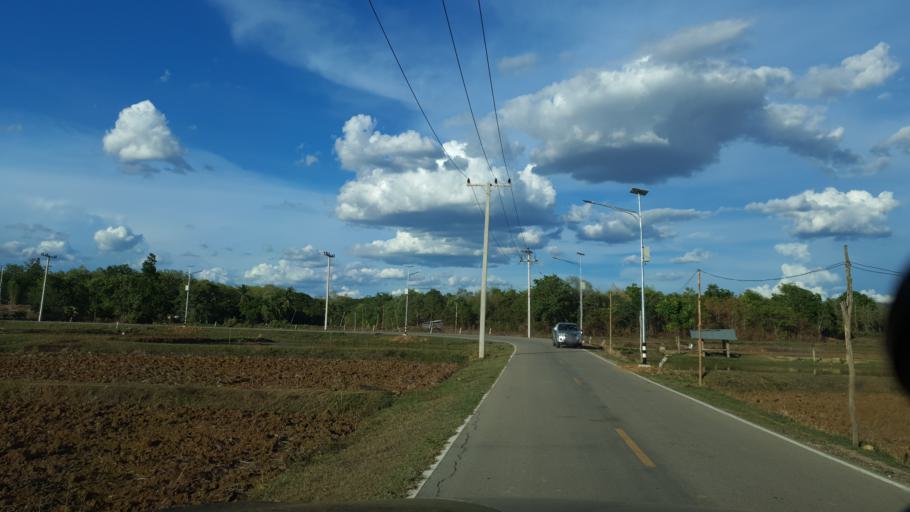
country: TH
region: Lampang
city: Sop Prap
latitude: 17.8919
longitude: 99.3143
